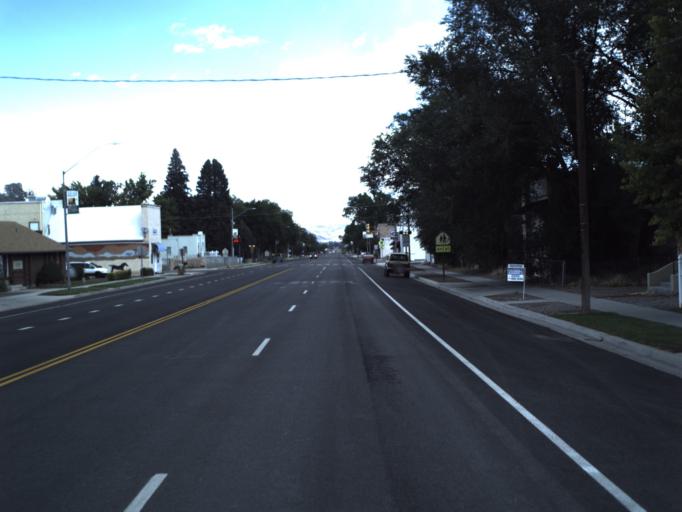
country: US
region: Utah
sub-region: Sevier County
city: Monroe
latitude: 38.6309
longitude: -112.1214
